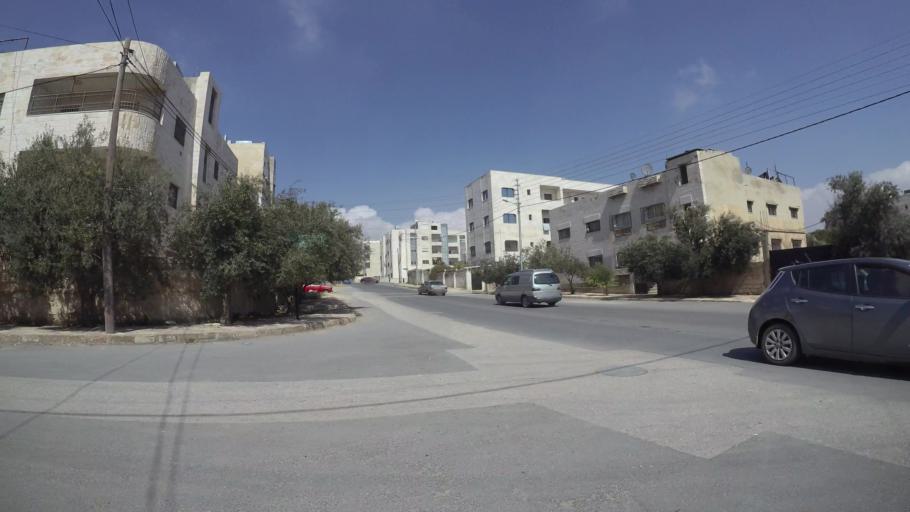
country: JO
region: Amman
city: Al Bunayyat ash Shamaliyah
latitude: 31.9010
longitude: 35.9056
